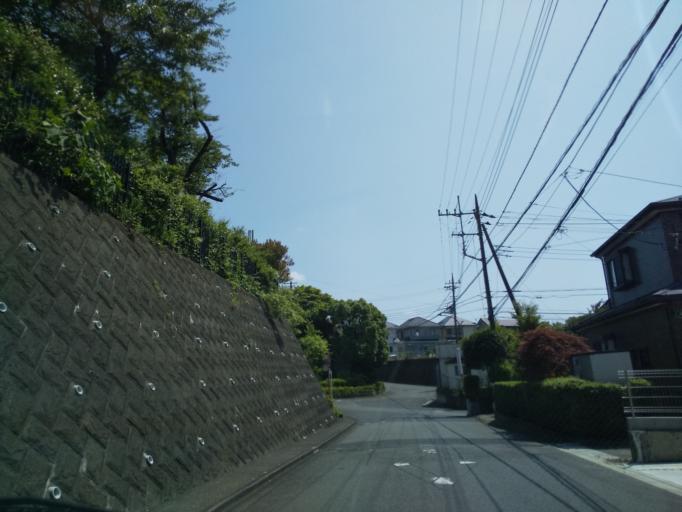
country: JP
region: Kanagawa
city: Zama
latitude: 35.5007
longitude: 139.3891
